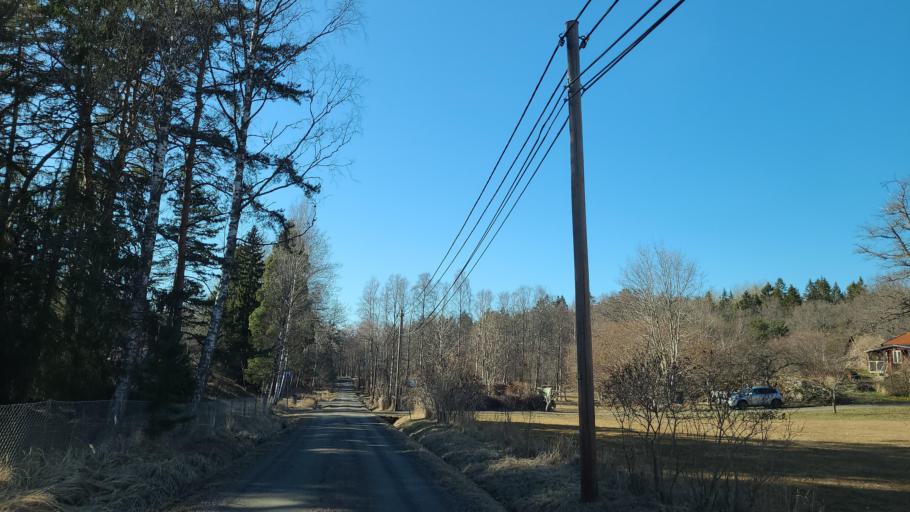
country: SE
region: Stockholm
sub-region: Varmdo Kommun
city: Holo
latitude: 59.3625
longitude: 18.6641
